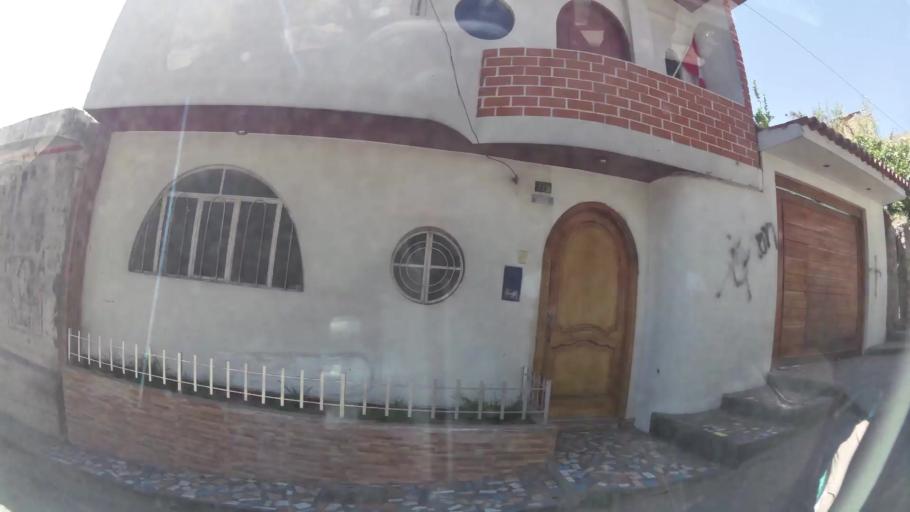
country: PE
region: Ayacucho
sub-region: Provincia de Huamanga
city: Carmen Alto
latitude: -13.1739
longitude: -74.2267
